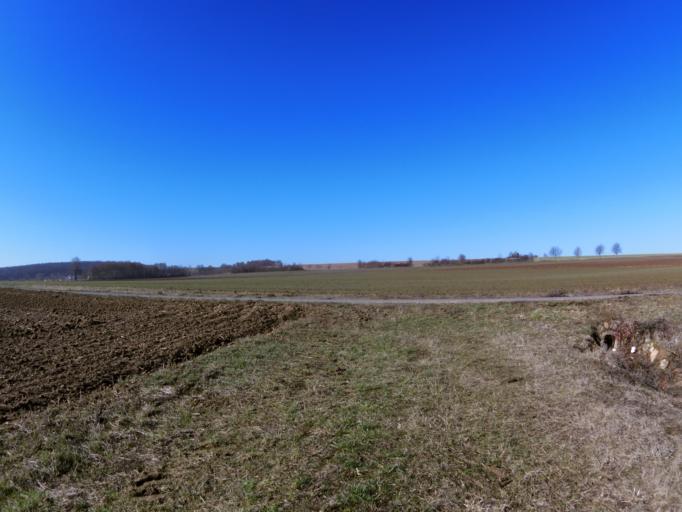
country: DE
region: Bavaria
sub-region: Regierungsbezirk Unterfranken
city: Estenfeld
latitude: 49.8389
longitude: 9.9931
